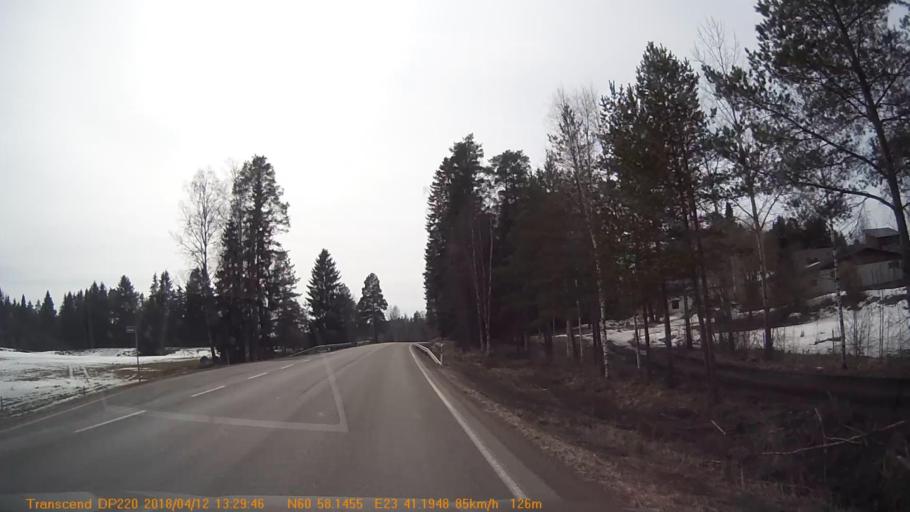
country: FI
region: Haeme
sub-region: Forssa
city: Forssa
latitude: 60.9690
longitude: 23.6864
